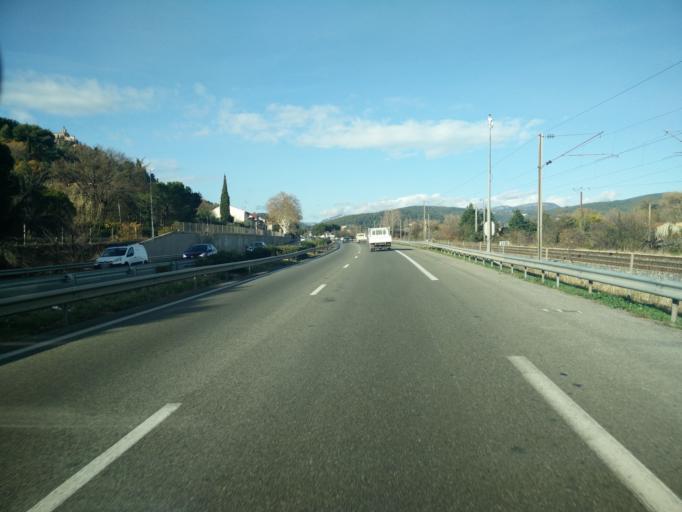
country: FR
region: Provence-Alpes-Cote d'Azur
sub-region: Departement du Var
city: Sollies-Ville
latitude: 43.1772
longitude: 6.0481
